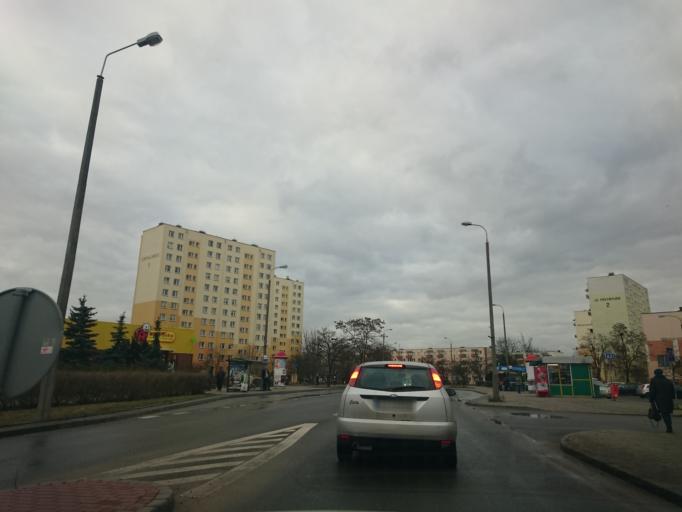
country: PL
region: Kujawsko-Pomorskie
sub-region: Powiat torunski
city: Lubicz Dolny
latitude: 53.0285
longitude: 18.6733
